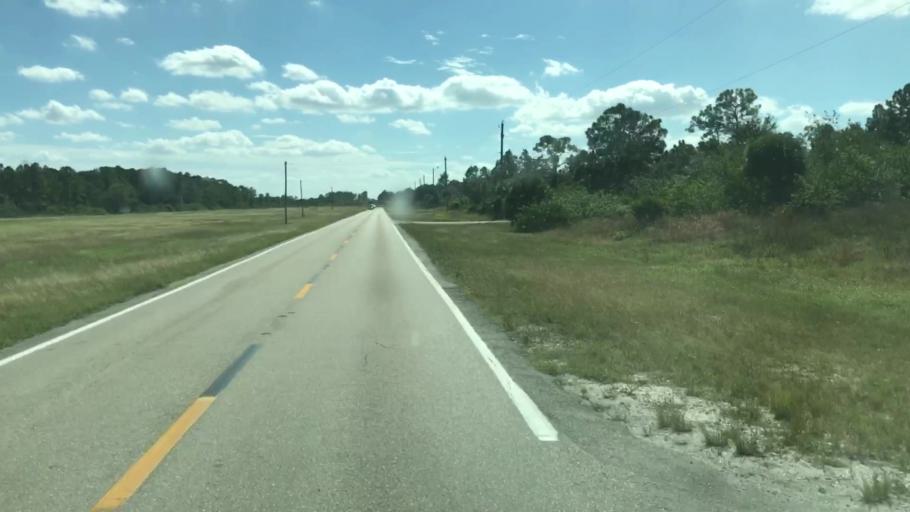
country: US
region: Florida
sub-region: Lee County
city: Lehigh Acres
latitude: 26.6509
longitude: -81.6634
